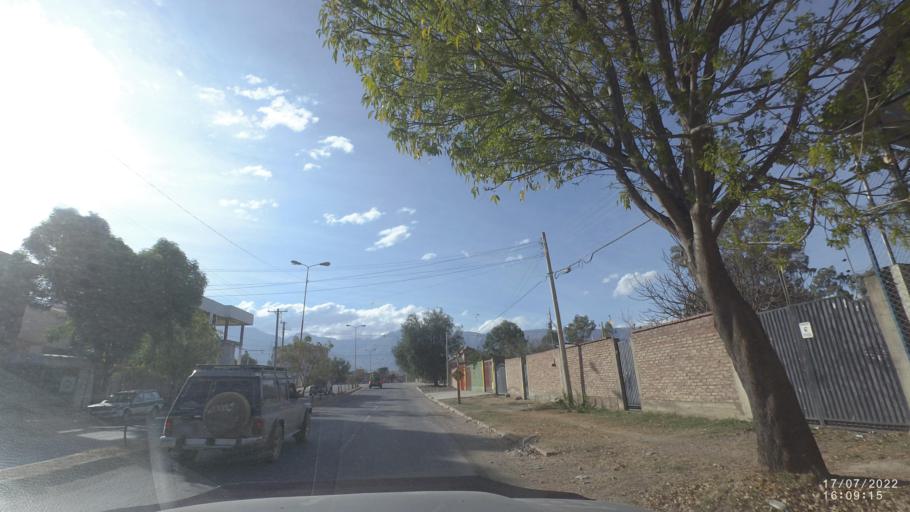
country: BO
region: Cochabamba
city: Cochabamba
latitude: -17.4016
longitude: -66.2736
